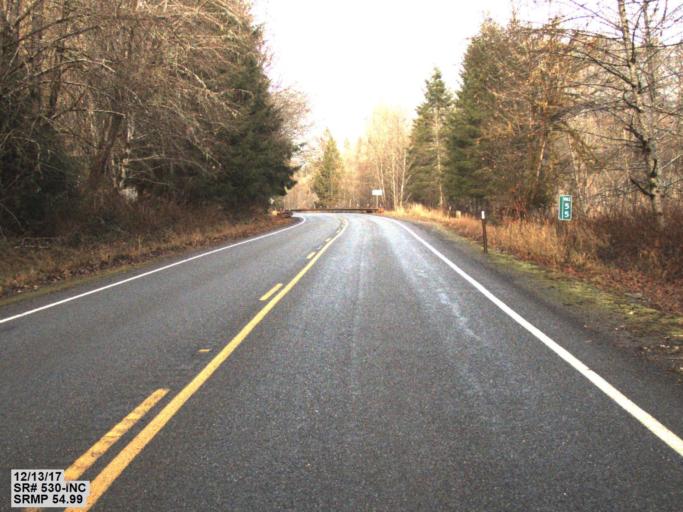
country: US
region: Washington
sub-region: Snohomish County
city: Darrington
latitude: 48.3282
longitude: -121.5513
